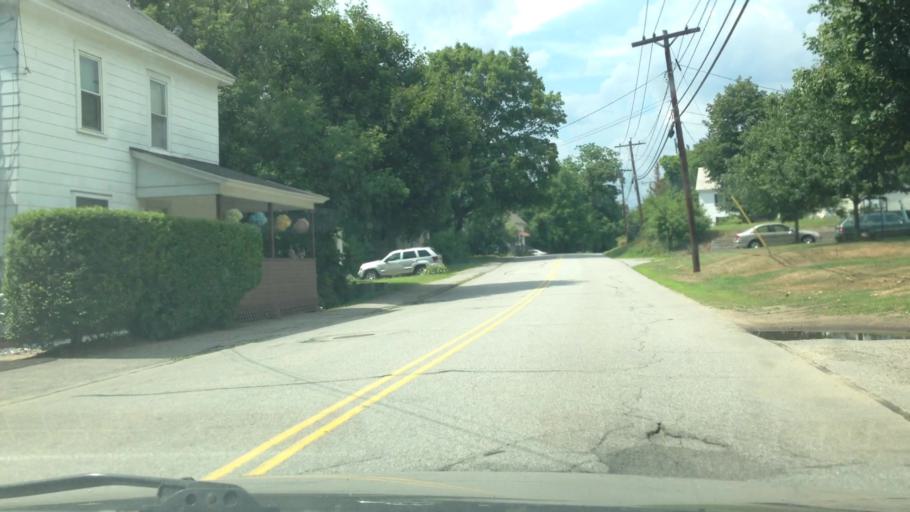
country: US
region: New Hampshire
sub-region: Cheshire County
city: Keene
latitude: 42.9265
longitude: -72.2632
